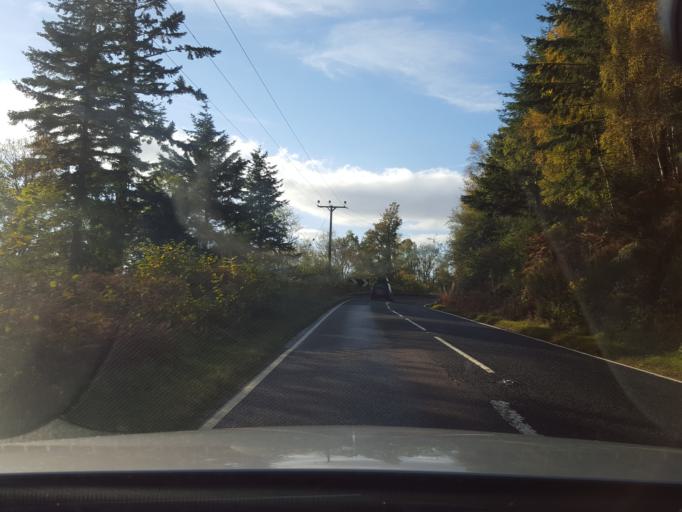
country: GB
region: Scotland
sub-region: Highland
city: Beauly
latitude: 57.2248
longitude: -4.5736
